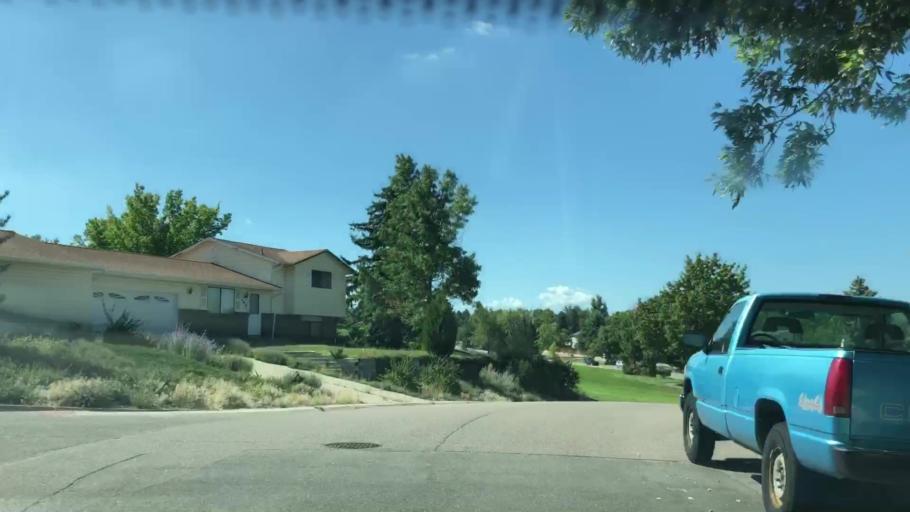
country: US
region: Colorado
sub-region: Douglas County
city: Acres Green
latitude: 39.5598
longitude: -104.8952
